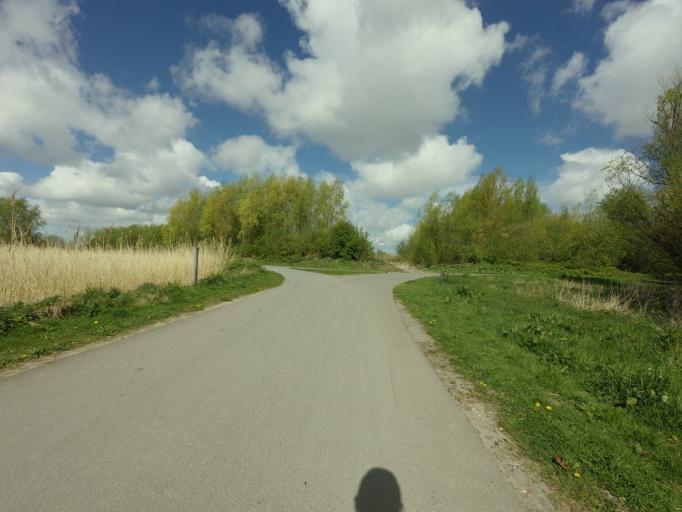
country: NL
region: South Holland
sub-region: Gemeente Lansingerland
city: Bleiswijk
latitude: 51.9795
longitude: 4.5409
